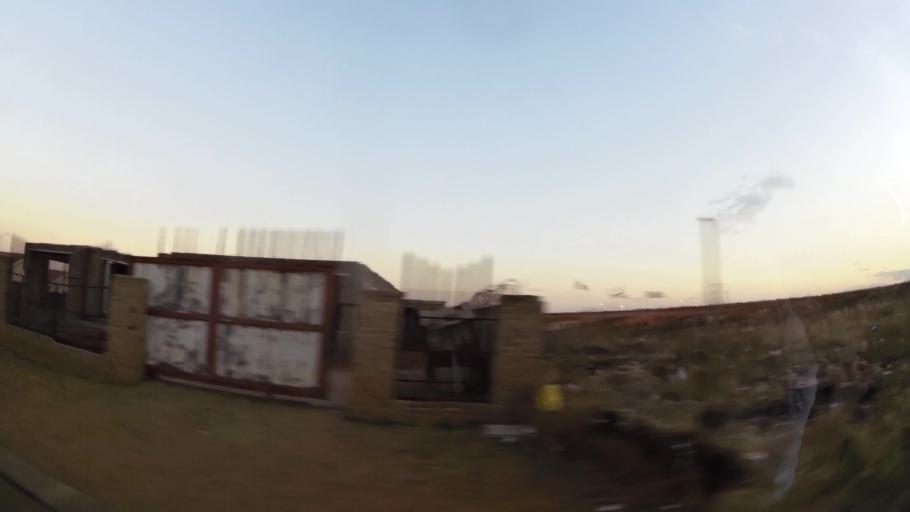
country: ZA
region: Gauteng
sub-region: West Rand District Municipality
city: Randfontein
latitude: -26.2125
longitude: 27.7110
